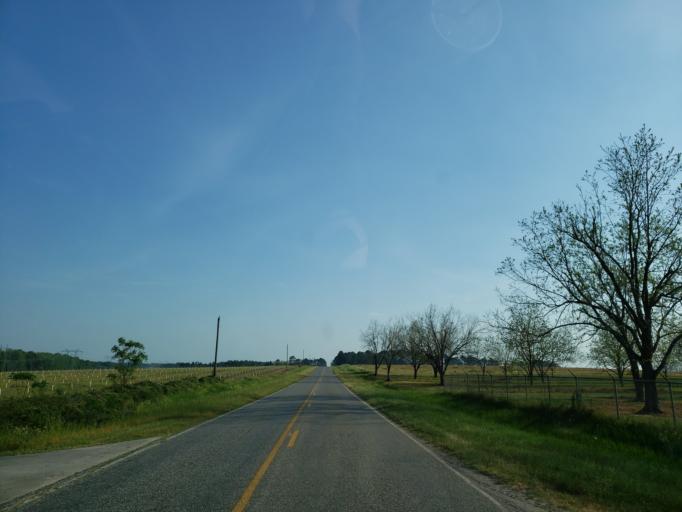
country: US
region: Georgia
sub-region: Tift County
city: Tifton
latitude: 31.5176
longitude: -83.5600
